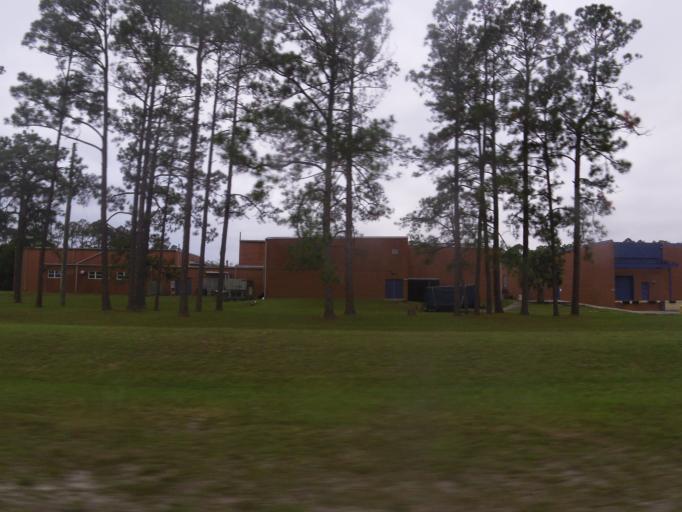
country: US
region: Florida
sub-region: Duval County
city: Baldwin
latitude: 30.2320
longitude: -81.8864
